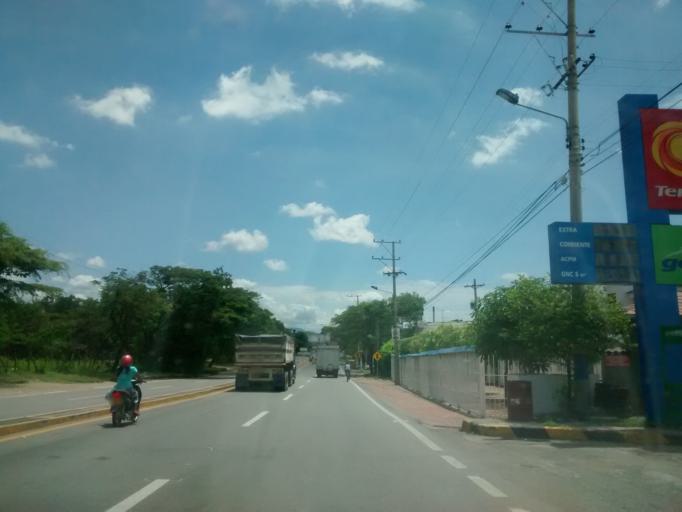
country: CO
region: Cundinamarca
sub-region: Girardot
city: Girardot City
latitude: 4.3177
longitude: -74.8038
